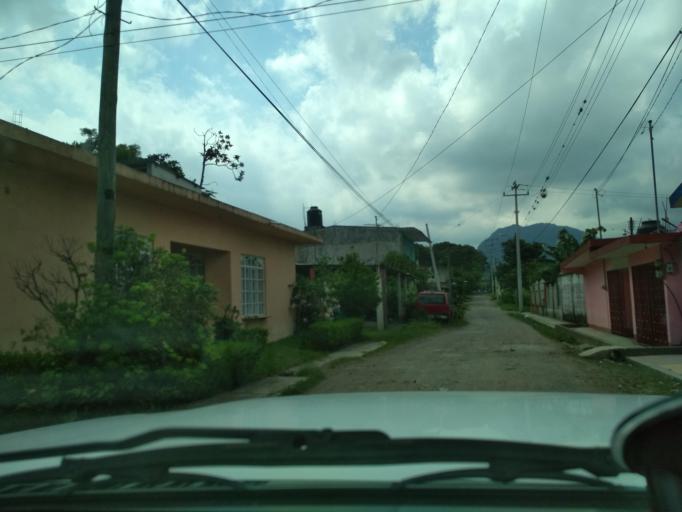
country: MX
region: Veracruz
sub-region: Ixtaczoquitlan
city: Buenavista
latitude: 18.8918
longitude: -97.0386
